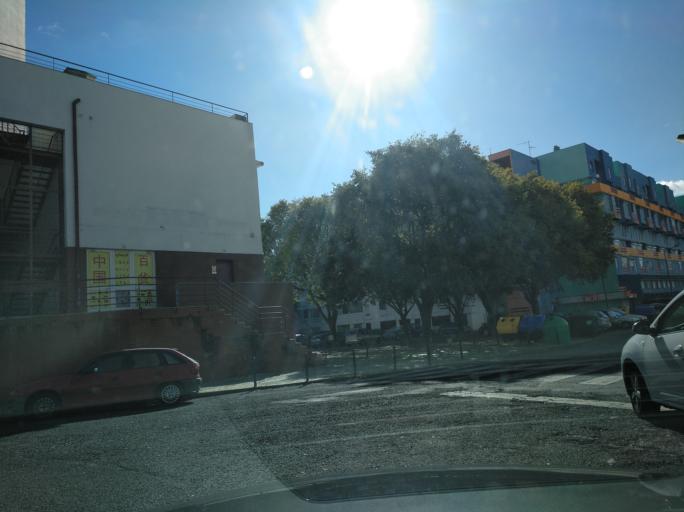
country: PT
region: Lisbon
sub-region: Lisbon
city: Lisbon
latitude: 38.7439
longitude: -9.1135
